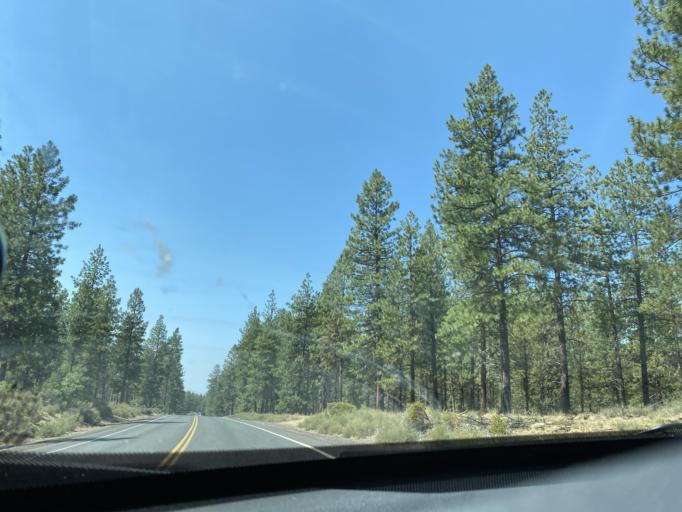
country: US
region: Oregon
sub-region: Deschutes County
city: Sunriver
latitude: 43.8910
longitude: -121.3875
